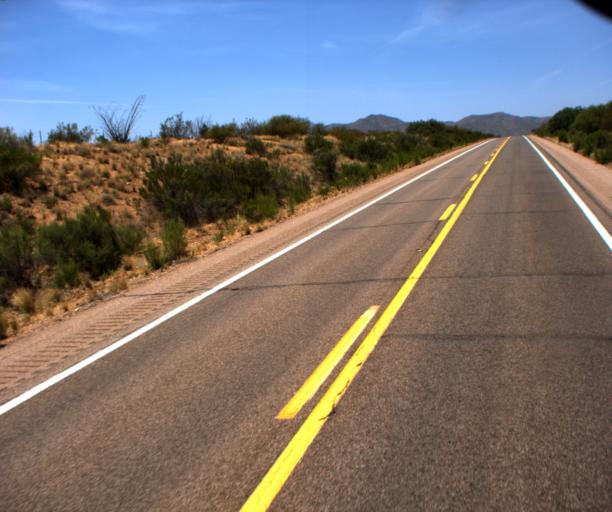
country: US
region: Arizona
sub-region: Gila County
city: Miami
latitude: 33.6142
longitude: -111.0258
